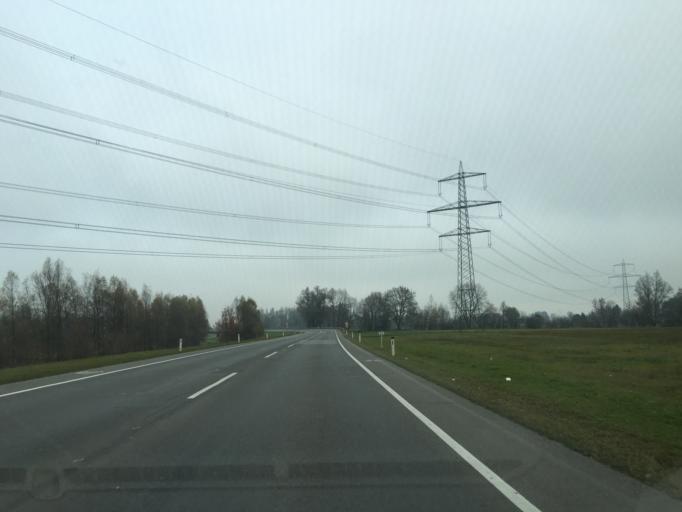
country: AT
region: Vorarlberg
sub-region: Politischer Bezirk Dornbirn
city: Hohenems
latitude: 47.3862
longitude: 9.6830
